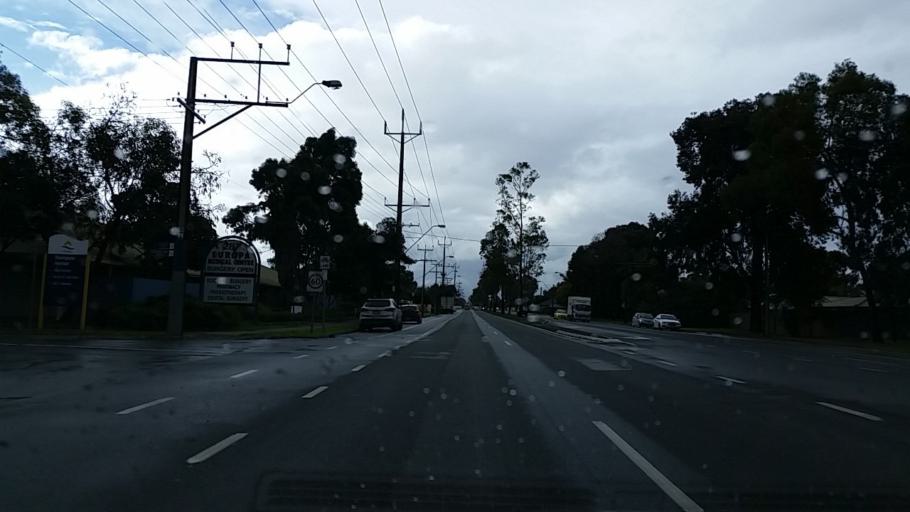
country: AU
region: South Australia
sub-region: Salisbury
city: Salisbury
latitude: -34.7781
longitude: 138.6273
